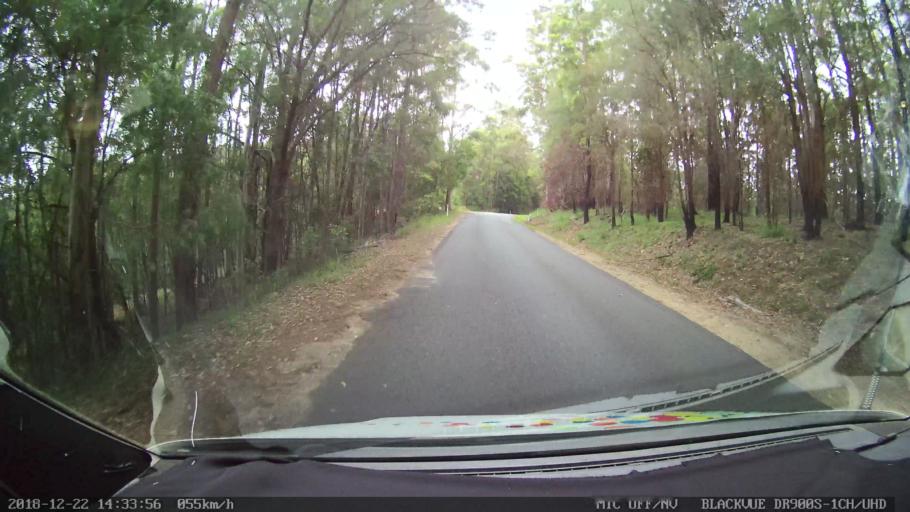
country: AU
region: New South Wales
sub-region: Bellingen
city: Dorrigo
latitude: -30.1165
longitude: 152.6221
